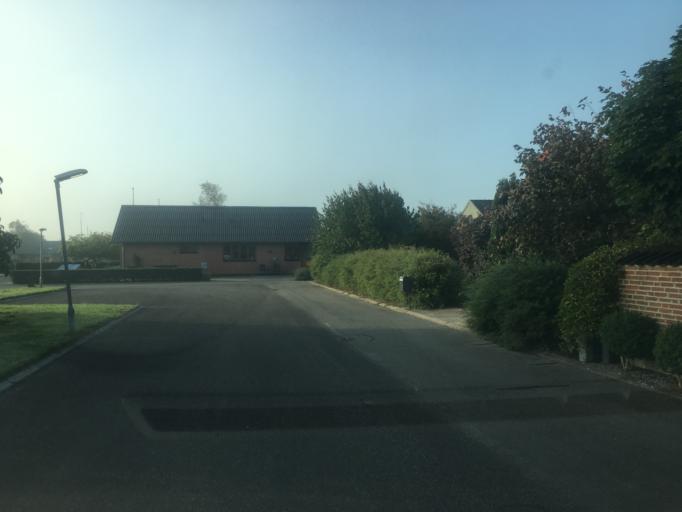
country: DK
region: South Denmark
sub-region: Tonder Kommune
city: Tonder
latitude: 54.9396
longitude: 8.8488
